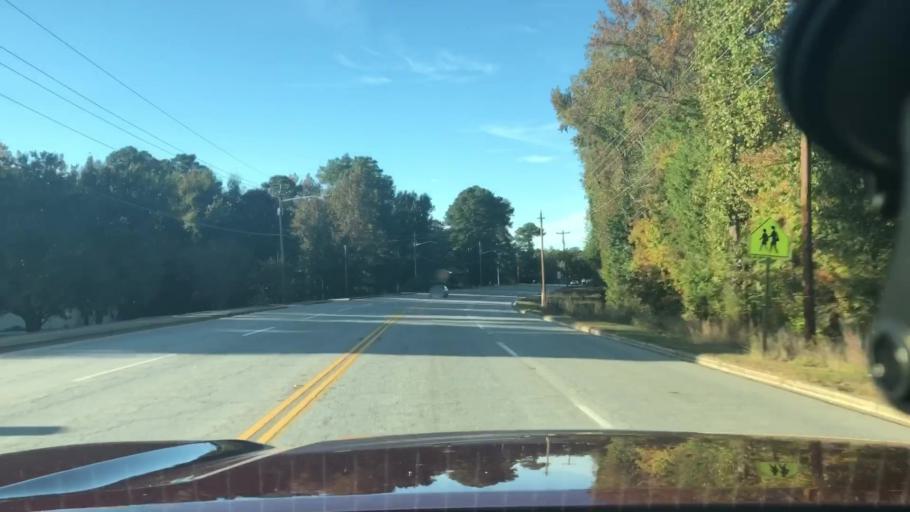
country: US
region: South Carolina
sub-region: Greenwood County
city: Greenwood
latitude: 34.2225
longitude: -82.1407
